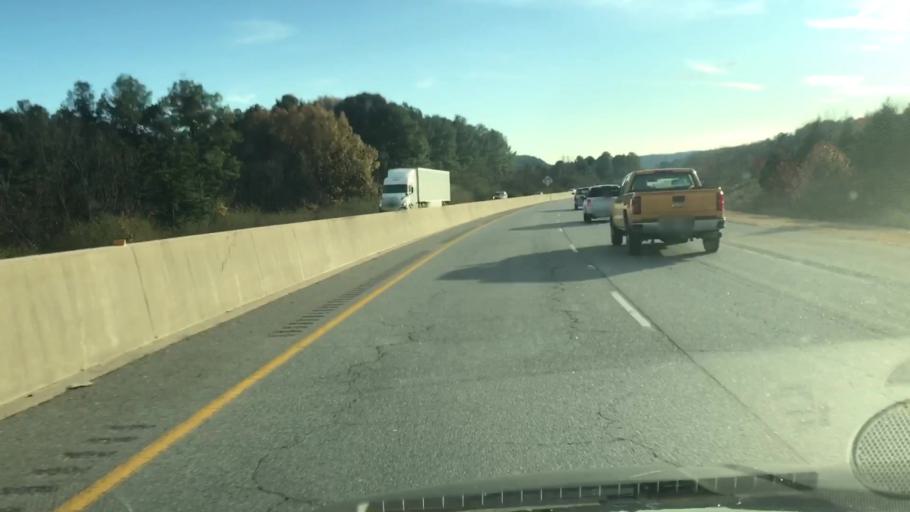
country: US
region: Arkansas
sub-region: Garland County
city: Hot Springs
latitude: 34.4940
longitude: -92.9761
